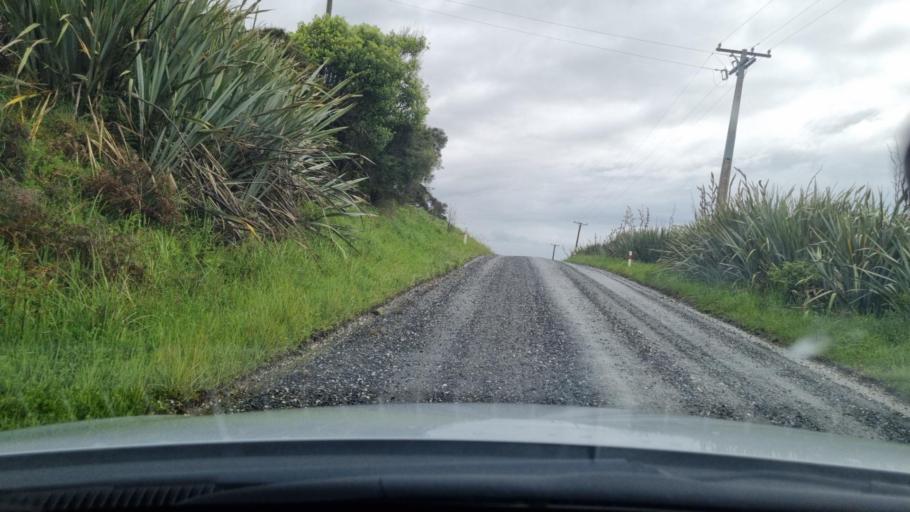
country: NZ
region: Southland
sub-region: Invercargill City
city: Bluff
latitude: -46.5261
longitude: 168.2701
